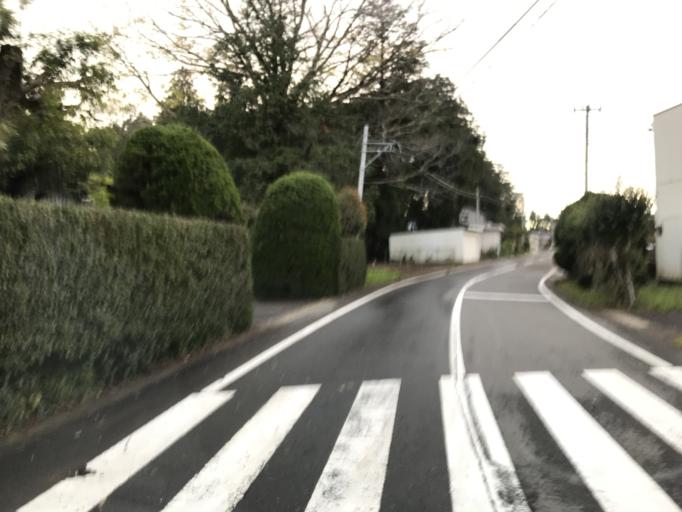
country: JP
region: Chiba
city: Yokaichiba
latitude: 35.7718
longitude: 140.4574
